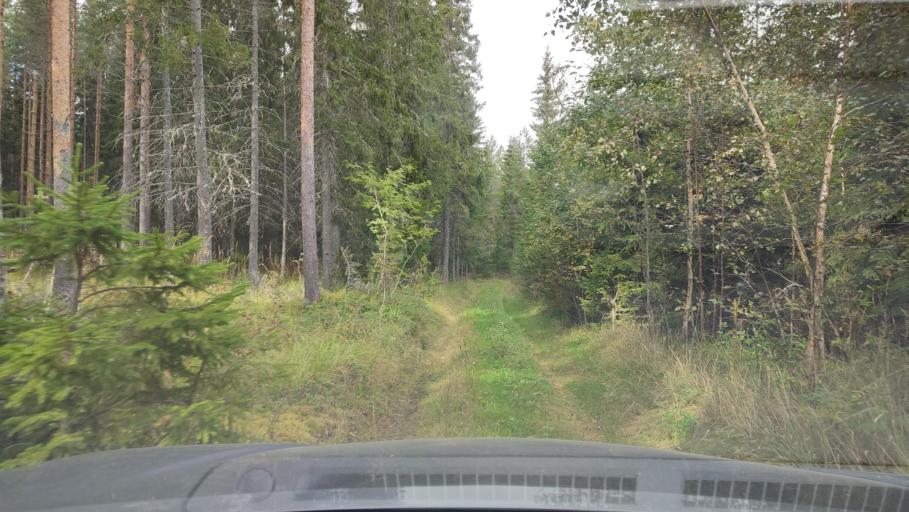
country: FI
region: Southern Ostrobothnia
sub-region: Suupohja
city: Karijoki
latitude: 62.2215
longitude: 21.6191
